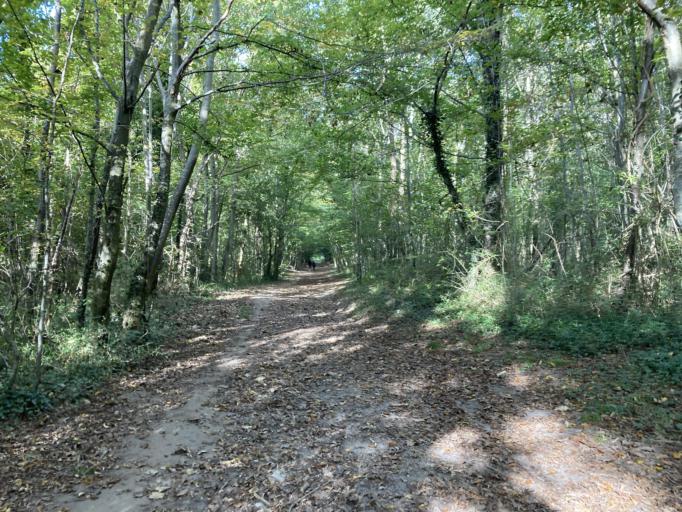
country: FR
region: Ile-de-France
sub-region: Departement des Yvelines
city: Saint-Germain-en-Laye
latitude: 48.9183
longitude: 2.0994
